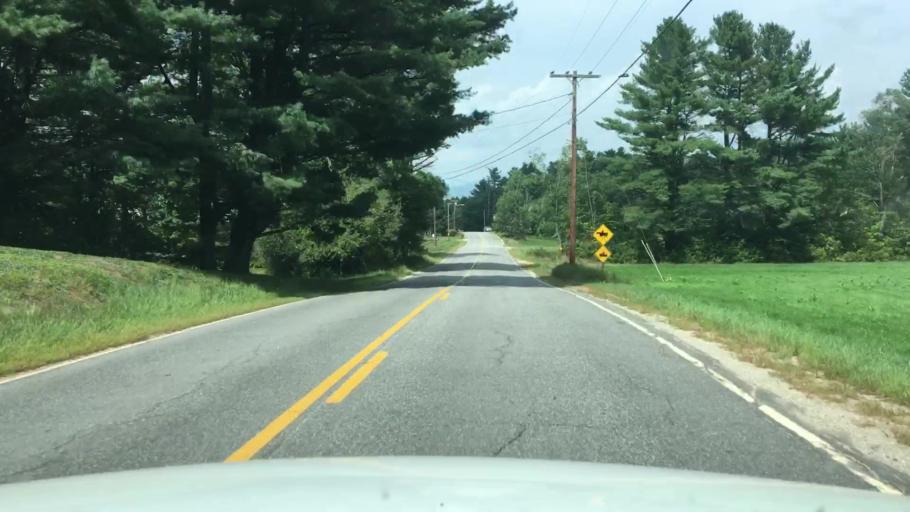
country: US
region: Maine
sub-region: Oxford County
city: Rumford
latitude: 44.6239
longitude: -70.7456
